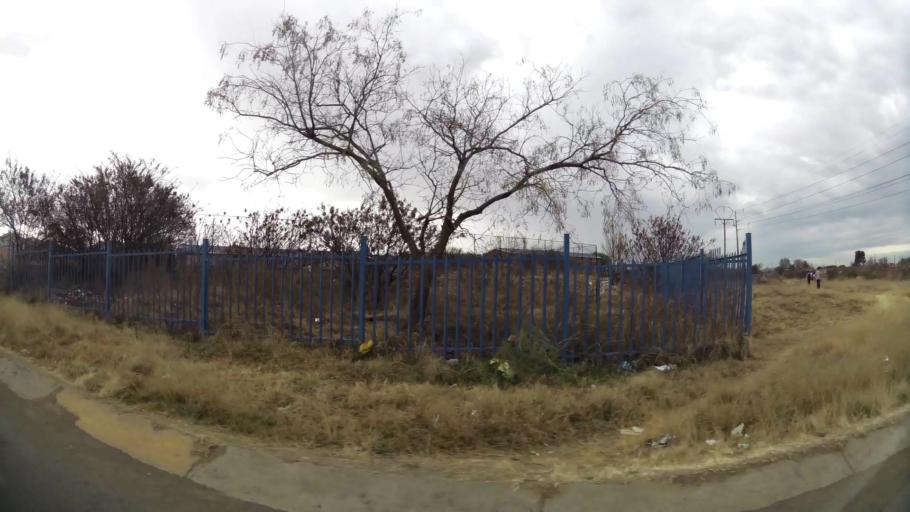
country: ZA
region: Orange Free State
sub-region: Fezile Dabi District Municipality
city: Kroonstad
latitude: -27.6561
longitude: 27.1989
